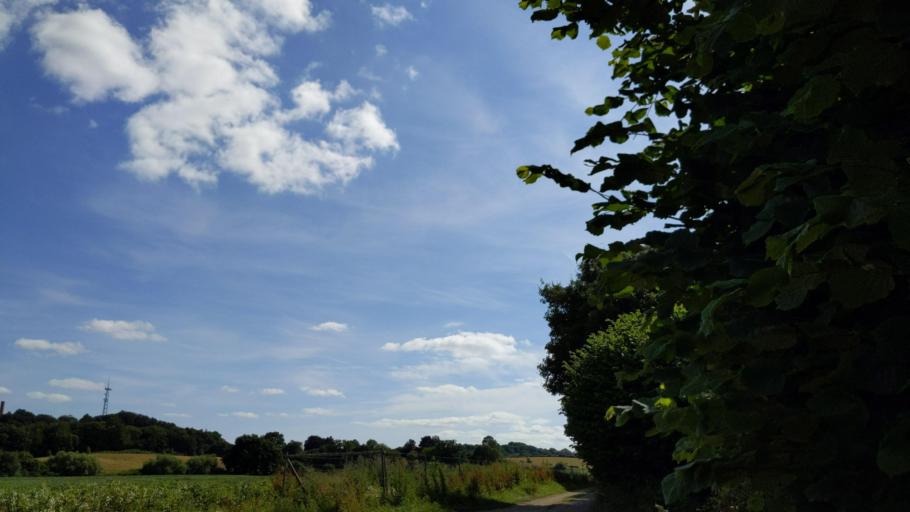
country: DE
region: Schleswig-Holstein
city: Kasseedorf
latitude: 54.1181
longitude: 10.7421
